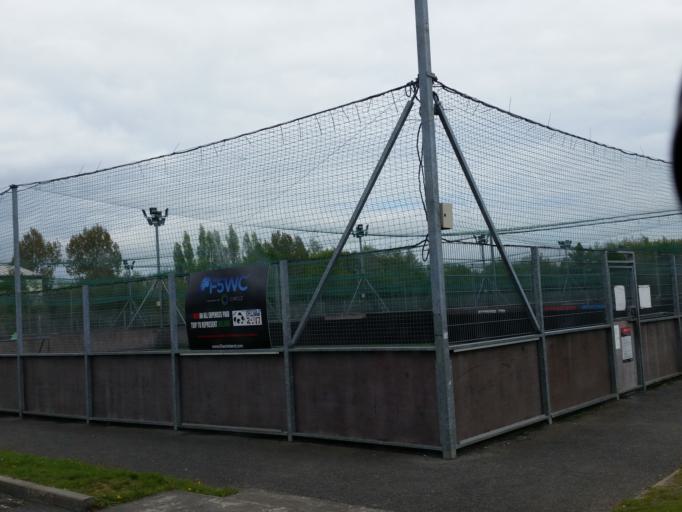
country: IE
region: Leinster
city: Beaumont
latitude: 53.3967
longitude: -6.2298
